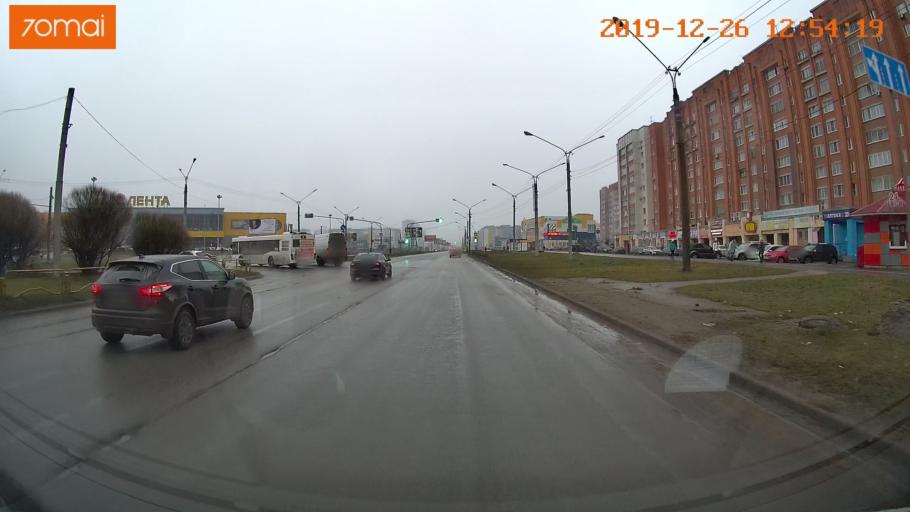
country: RU
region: Vologda
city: Cherepovets
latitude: 59.0939
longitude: 37.9138
